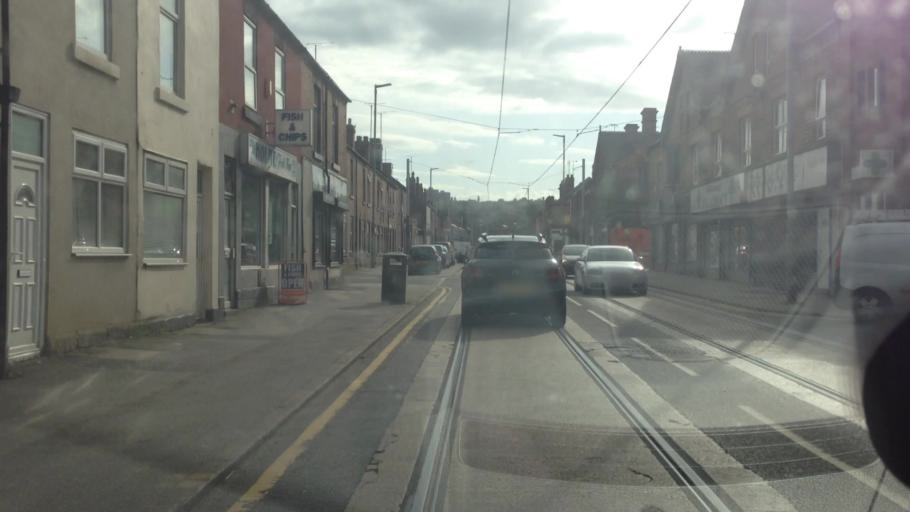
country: GB
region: England
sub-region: Sheffield
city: Sheffield
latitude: 53.4019
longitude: -1.5030
